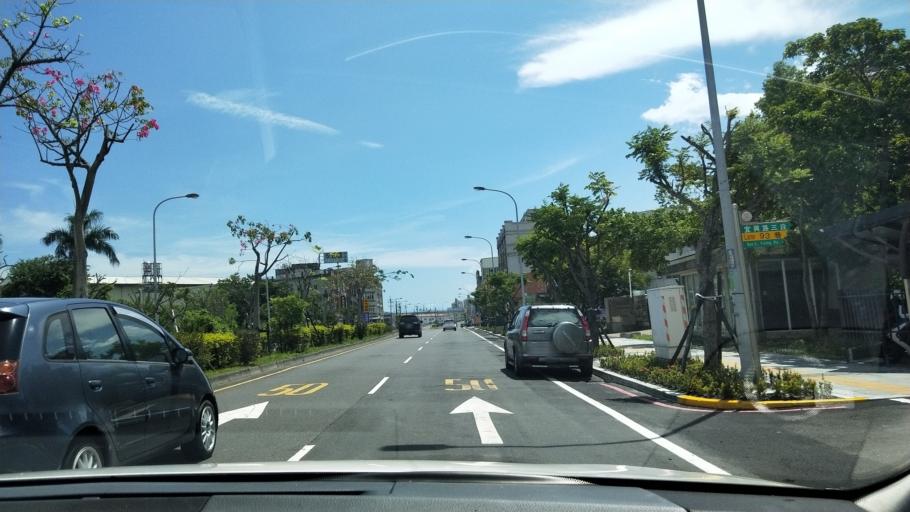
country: TW
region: Taiwan
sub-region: Yilan
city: Yilan
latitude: 24.7690
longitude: 121.7596
